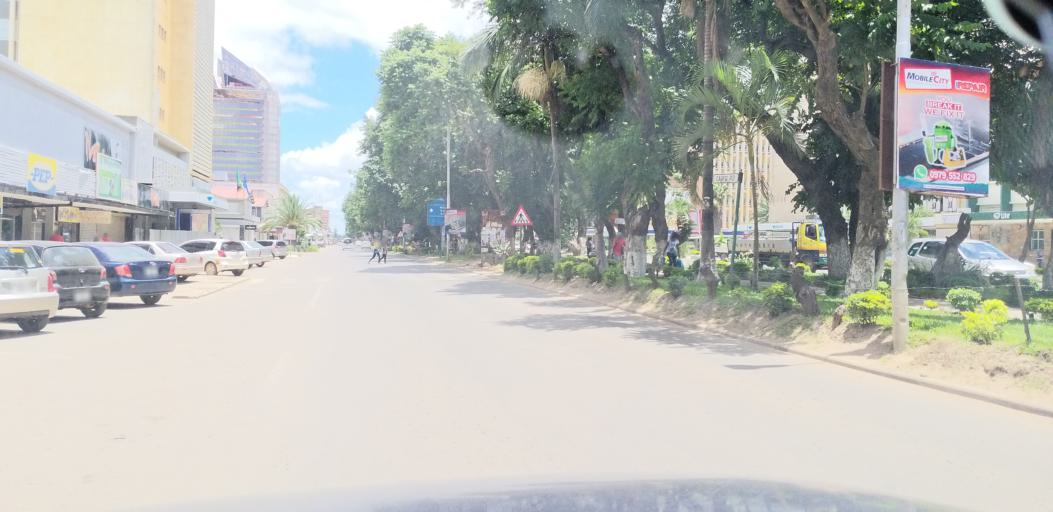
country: ZM
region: Lusaka
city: Lusaka
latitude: -15.4211
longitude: 28.2823
